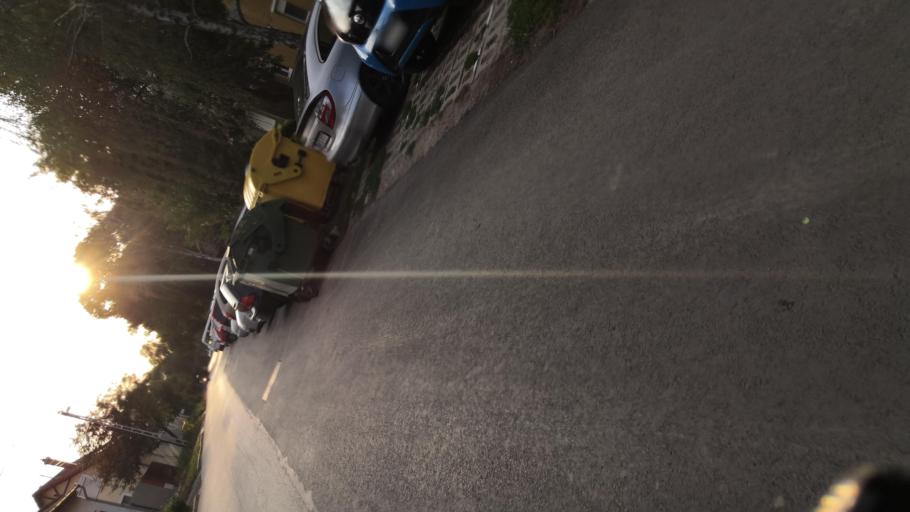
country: HU
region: Csongrad
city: Szeged
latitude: 46.2771
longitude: 20.1573
